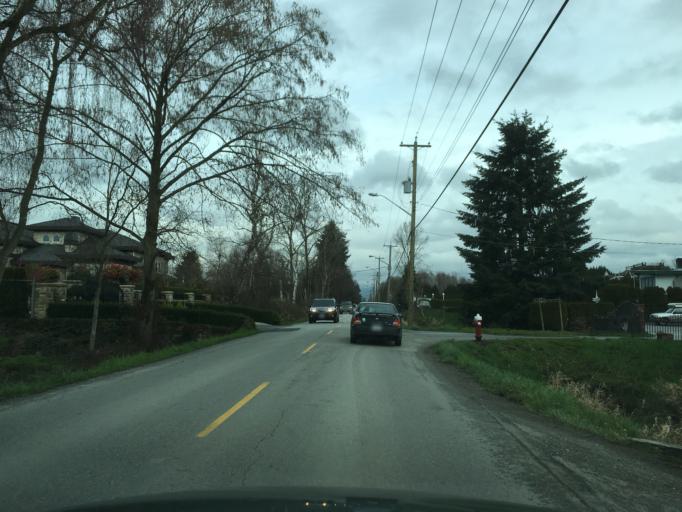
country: CA
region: British Columbia
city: Ladner
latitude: 49.1497
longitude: -123.0692
